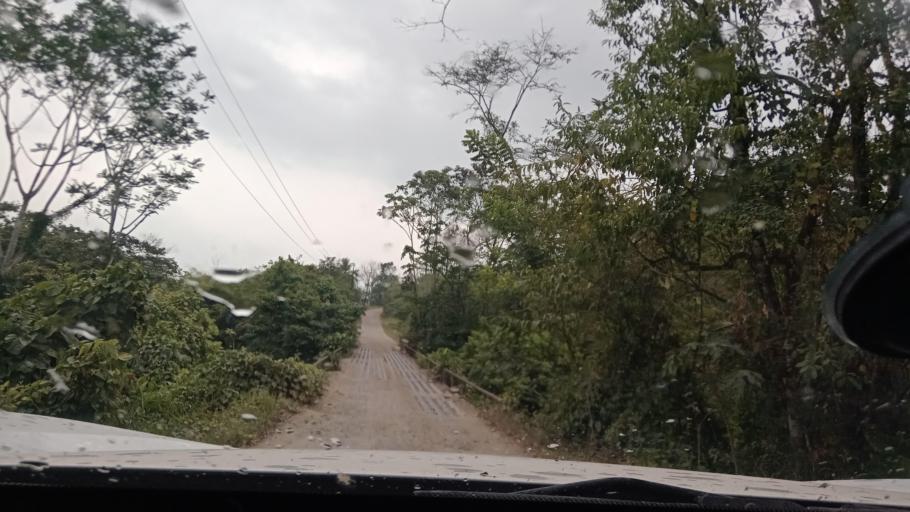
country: MX
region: Veracruz
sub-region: Uxpanapa
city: Poblado 10
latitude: 17.4489
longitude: -94.0827
